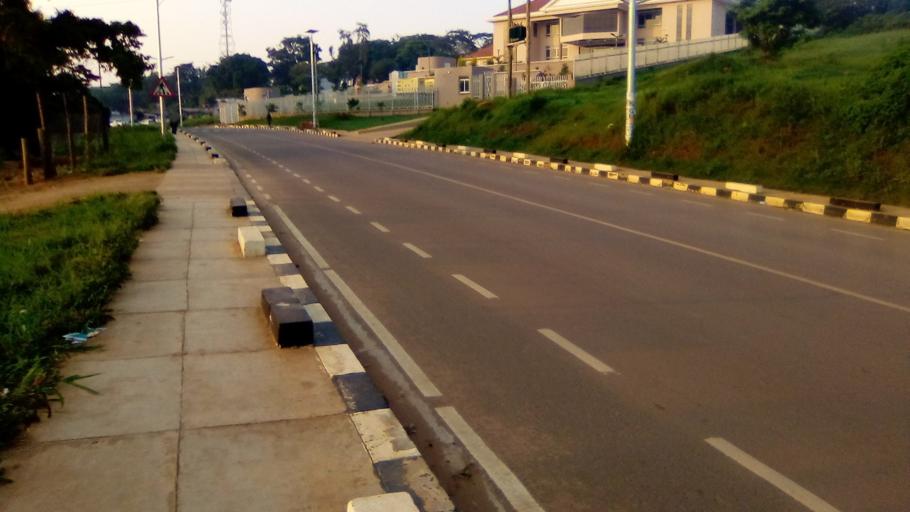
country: UG
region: Central Region
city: Masaka
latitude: -0.3386
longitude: 31.7377
